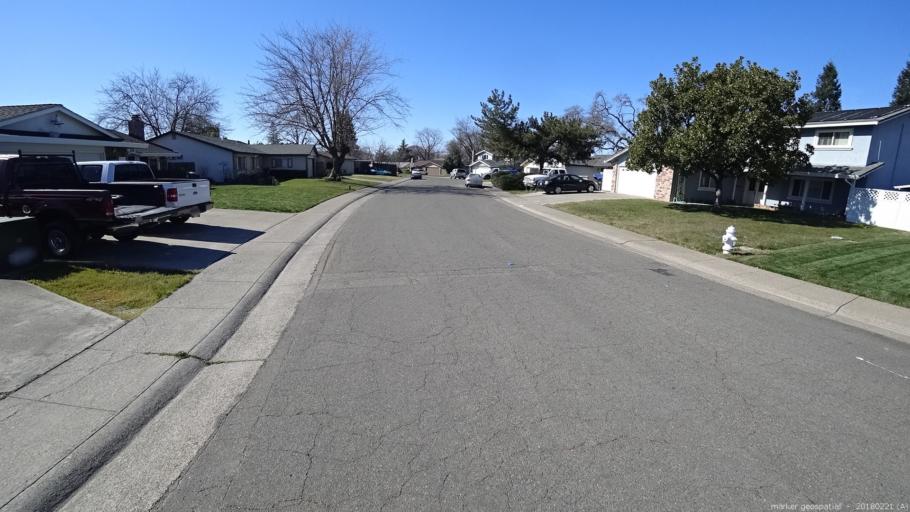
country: US
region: California
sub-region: Sacramento County
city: Citrus Heights
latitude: 38.6928
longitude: -121.2591
